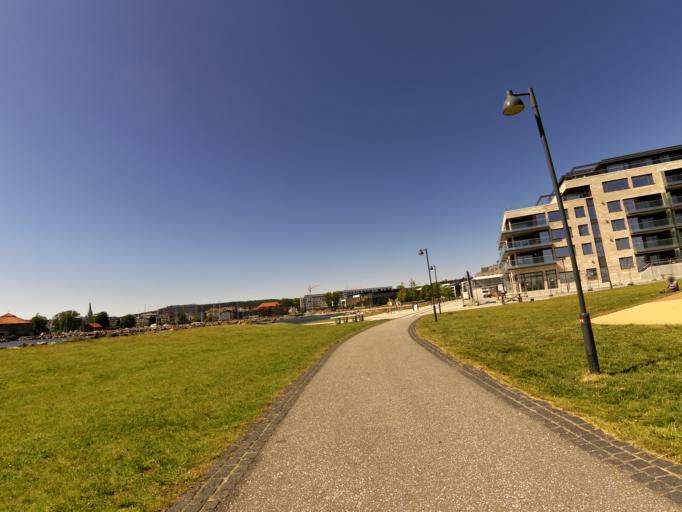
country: NO
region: Vest-Agder
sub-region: Kristiansand
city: Kristiansand
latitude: 58.1439
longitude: 8.0103
